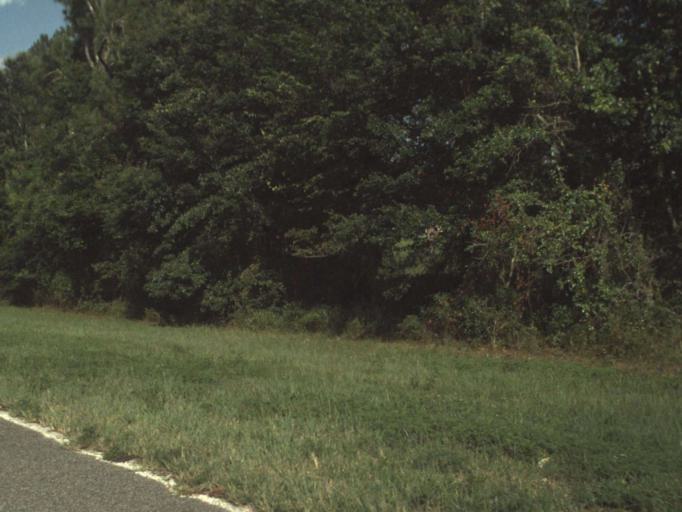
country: US
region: Florida
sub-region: Sumter County
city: Bushnell
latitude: 28.5599
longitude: -82.0402
